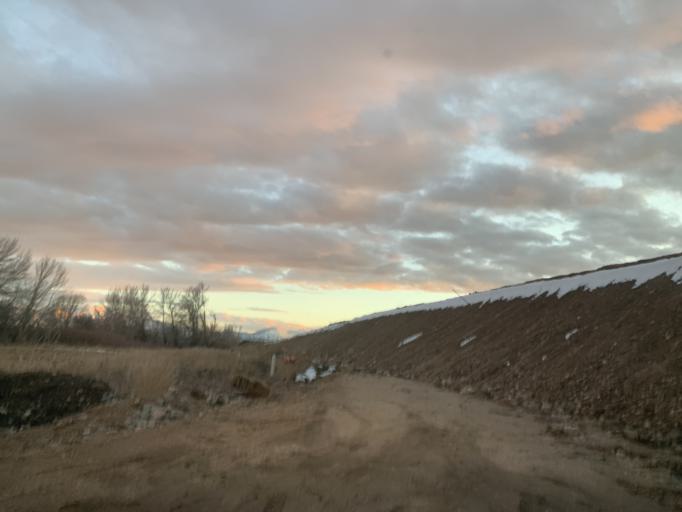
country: US
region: Utah
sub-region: Utah County
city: Provo
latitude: 40.2399
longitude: -111.7157
